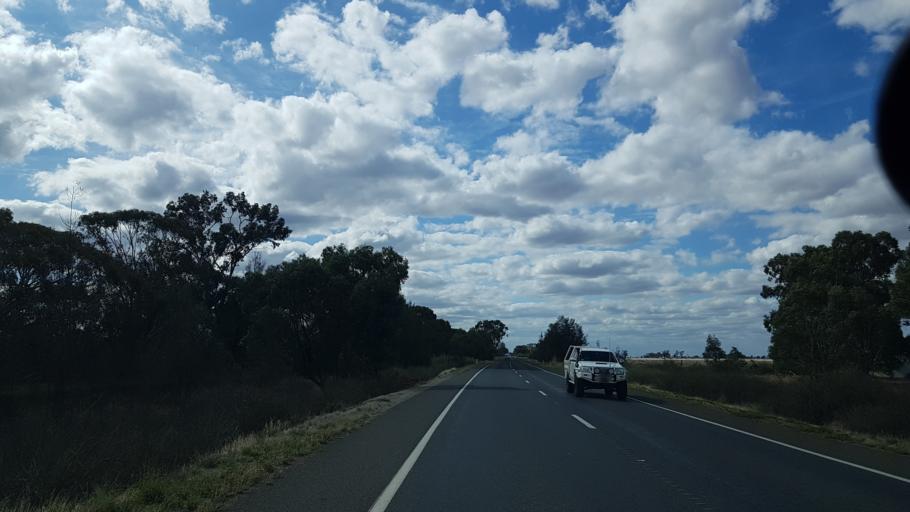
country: AU
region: Victoria
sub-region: Swan Hill
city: Swan Hill
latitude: -35.9881
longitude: 143.9460
